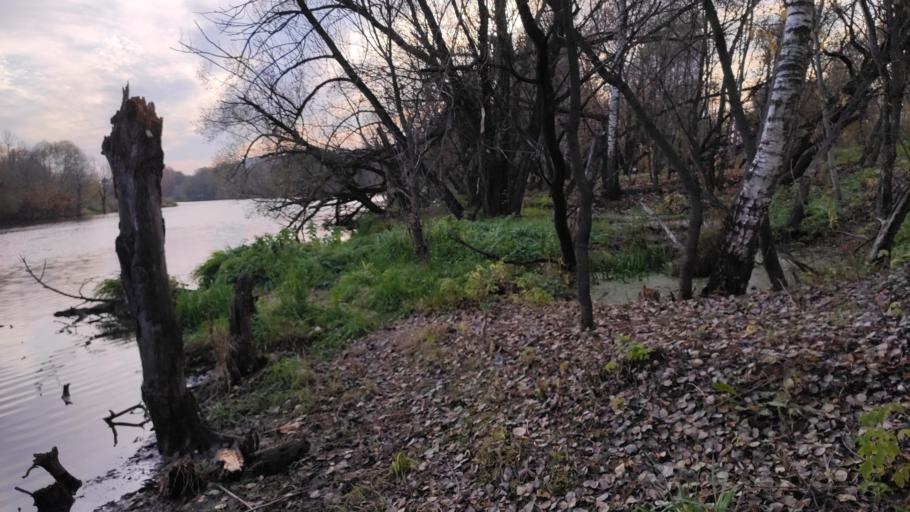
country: RU
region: Moskovskaya
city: Noginsk
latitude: 55.8688
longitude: 38.4531
